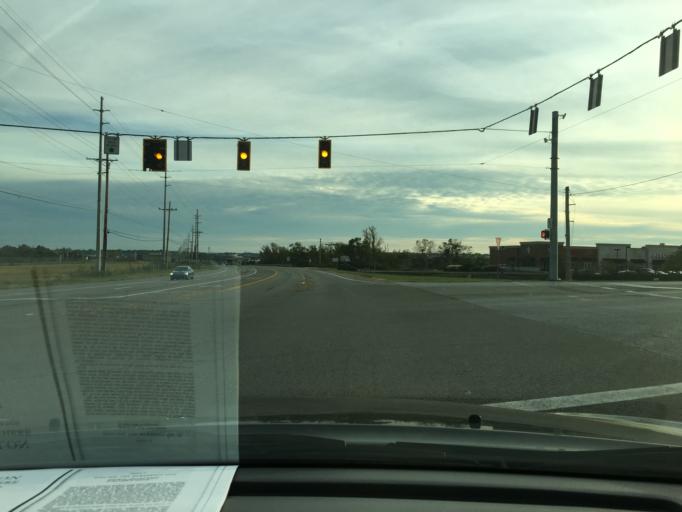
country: US
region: Ohio
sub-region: Butler County
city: Beckett Ridge
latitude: 39.3628
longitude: -84.4602
